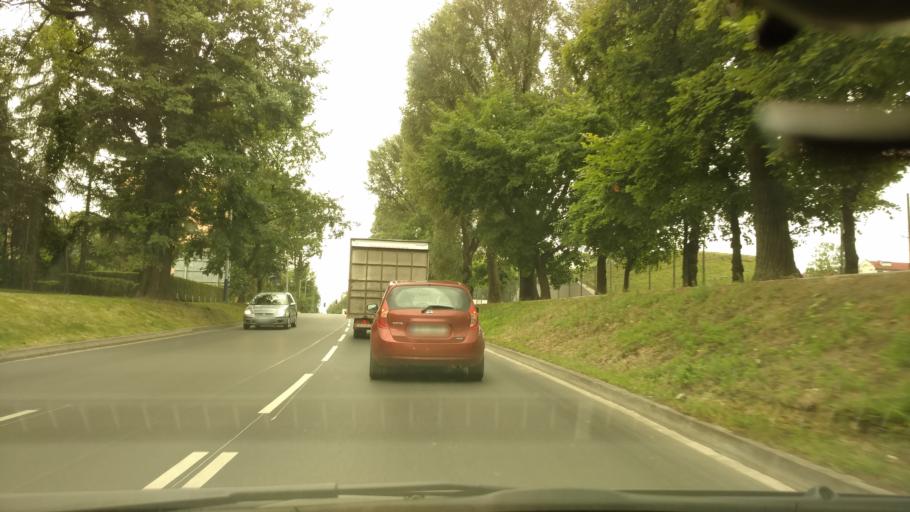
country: PL
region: Lesser Poland Voivodeship
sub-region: Krakow
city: Krakow
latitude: 50.0907
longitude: 19.9392
